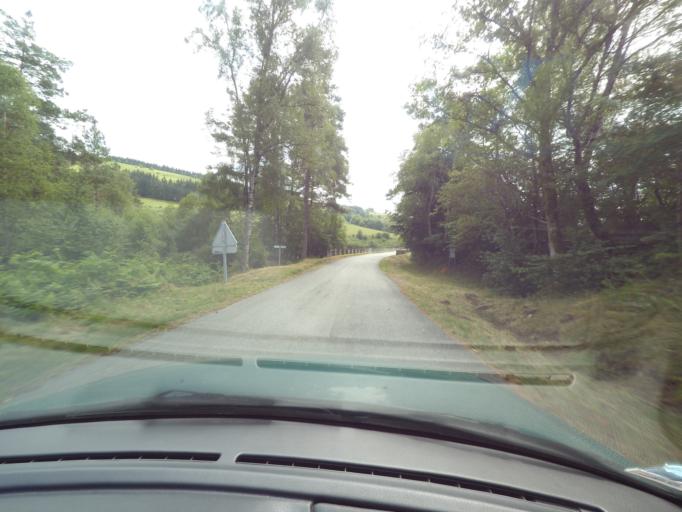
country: FR
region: Limousin
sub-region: Departement de la Correze
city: Bugeat
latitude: 45.7326
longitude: 1.9962
